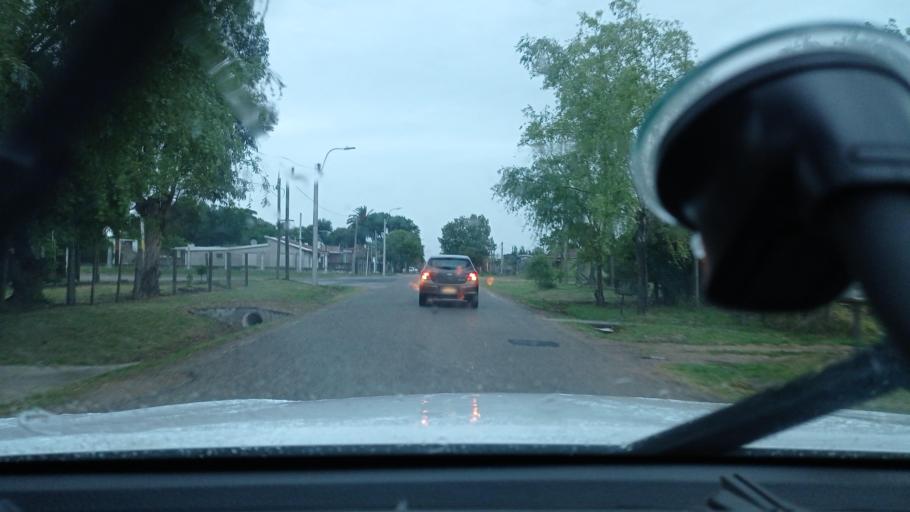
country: UY
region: Canelones
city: Joaquin Suarez
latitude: -34.7562
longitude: -56.0135
